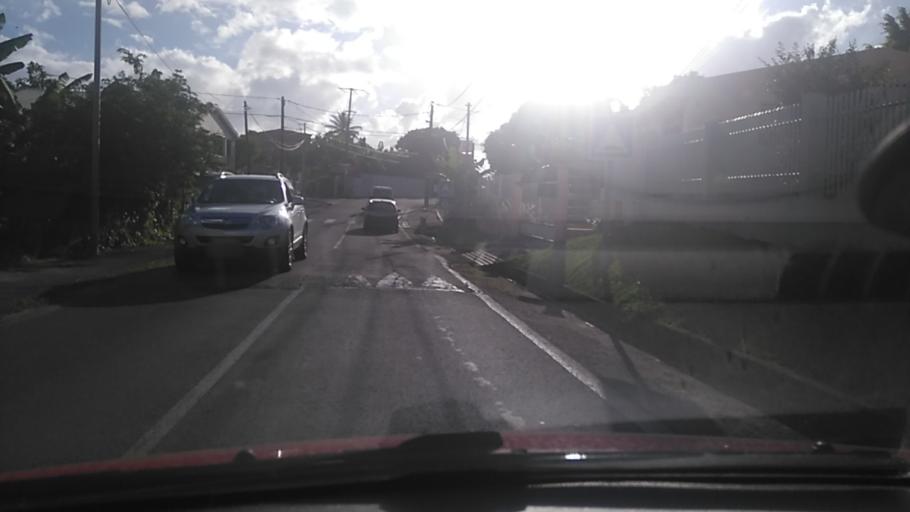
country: MQ
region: Martinique
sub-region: Martinique
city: Saint-Esprit
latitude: 14.5671
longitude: -60.9470
